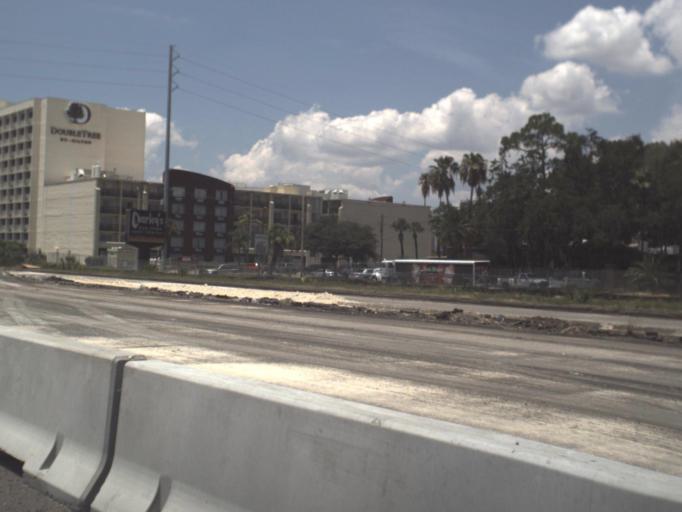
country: US
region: Florida
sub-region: Hillsborough County
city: Tampa
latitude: 27.9506
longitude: -82.5189
